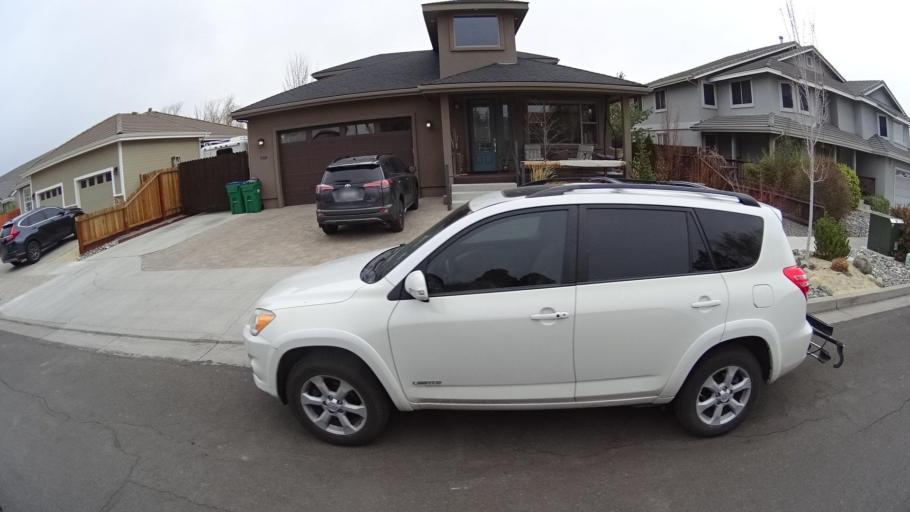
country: US
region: Nevada
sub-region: Washoe County
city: Reno
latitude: 39.5441
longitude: -119.8235
